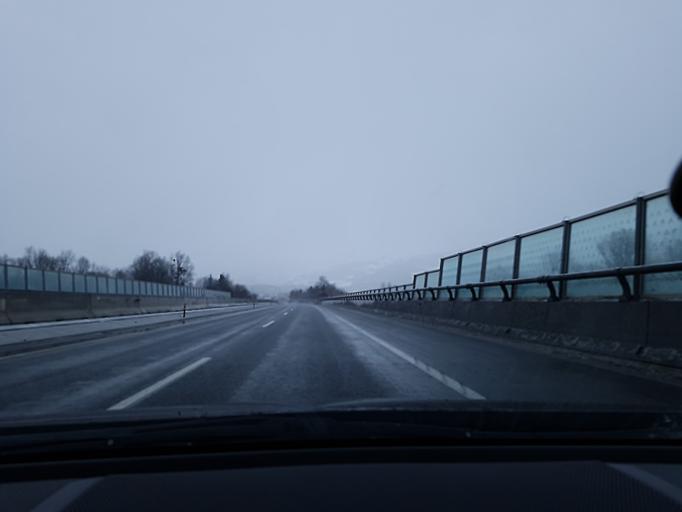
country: AT
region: Salzburg
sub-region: Politischer Bezirk Hallein
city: Kuchl
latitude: 47.6342
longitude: 13.1330
